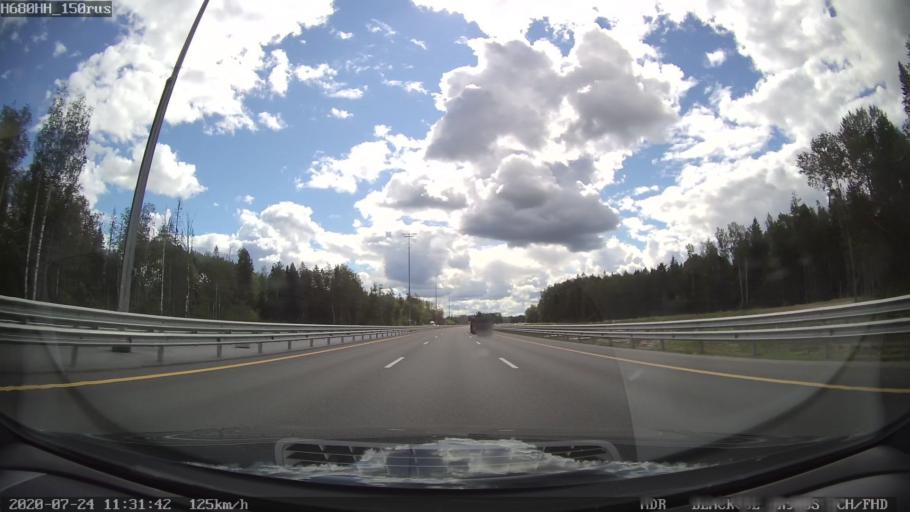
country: RU
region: Leningrad
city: Krasnyy Bor
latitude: 59.6524
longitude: 30.6440
